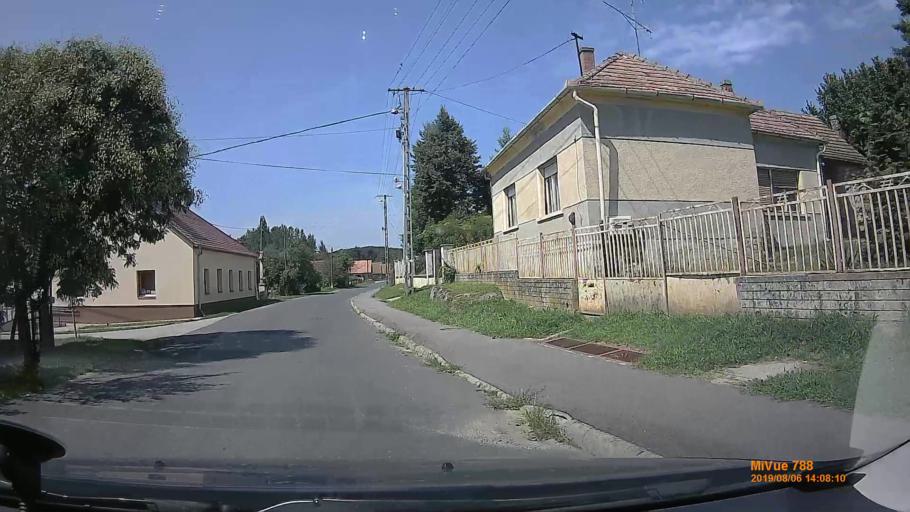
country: HU
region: Zala
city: Zalakomar
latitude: 46.5321
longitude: 17.0865
